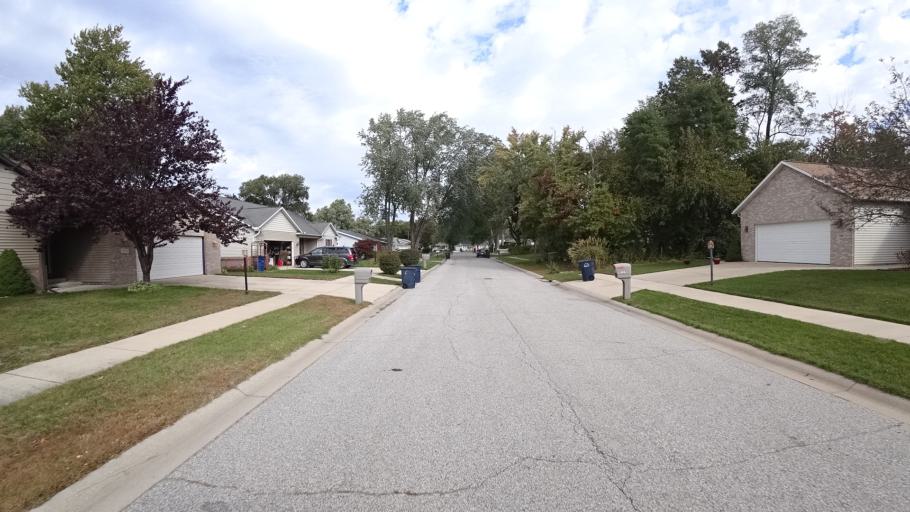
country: US
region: Indiana
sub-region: LaPorte County
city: Trail Creek
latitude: 41.6999
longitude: -86.8656
